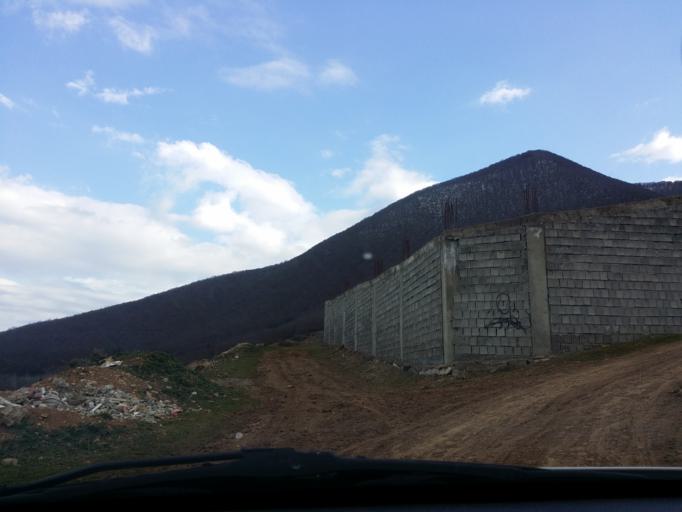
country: IR
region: Mazandaran
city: `Abbasabad
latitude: 36.5002
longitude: 51.1808
